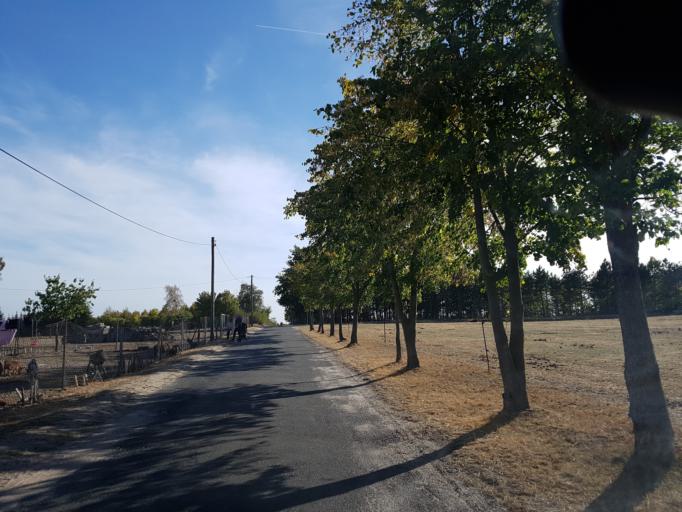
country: DE
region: Saxony-Anhalt
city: Jessen
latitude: 51.8019
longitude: 12.9931
